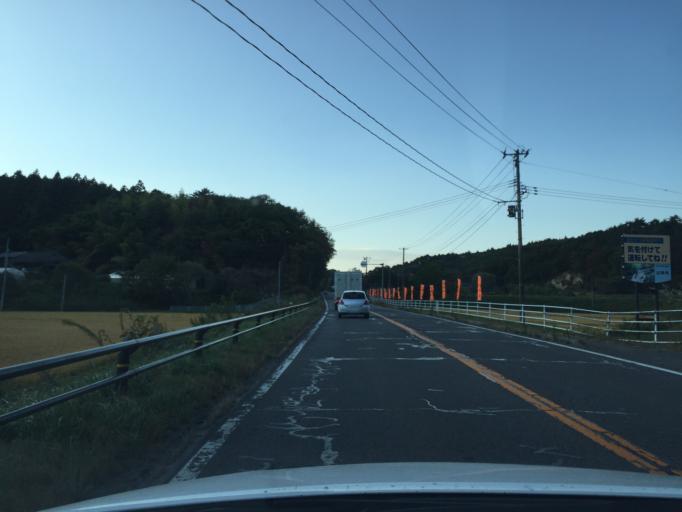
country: JP
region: Fukushima
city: Ishikawa
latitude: 37.2676
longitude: 140.5538
